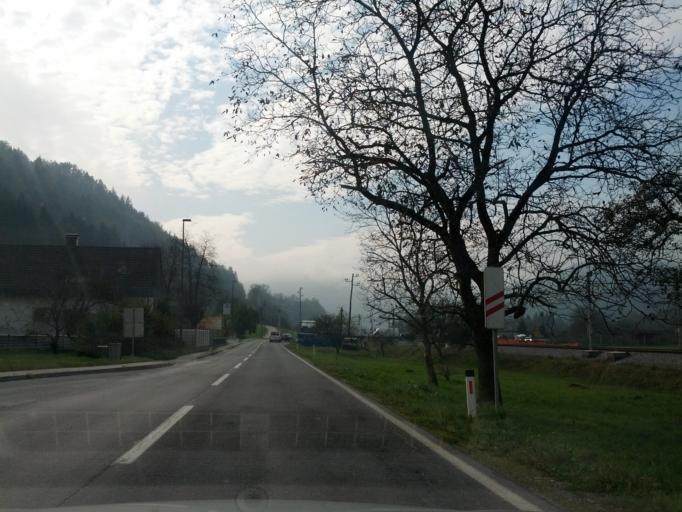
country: SI
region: Litija
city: Litija
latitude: 46.0766
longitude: 14.8251
